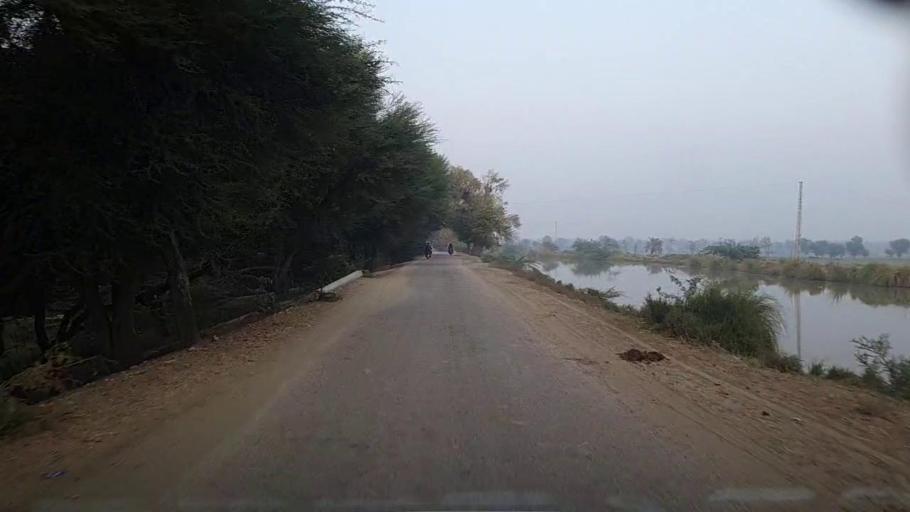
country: PK
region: Sindh
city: Bozdar
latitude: 27.0520
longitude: 68.5974
